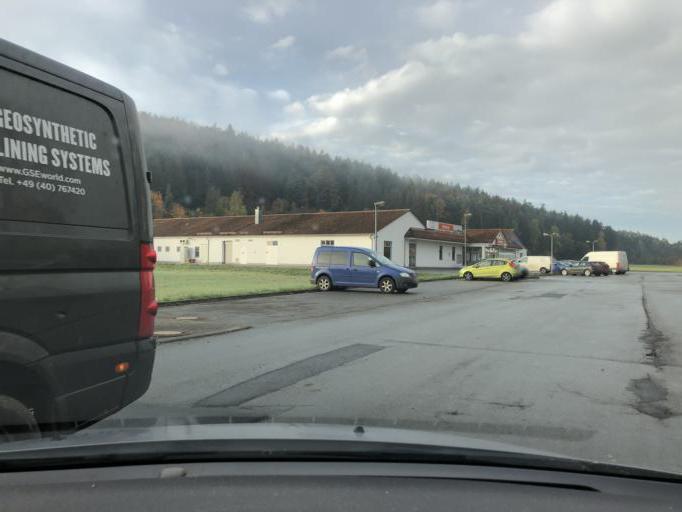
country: DE
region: Thuringia
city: Hildburghausen
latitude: 50.4207
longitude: 10.7102
